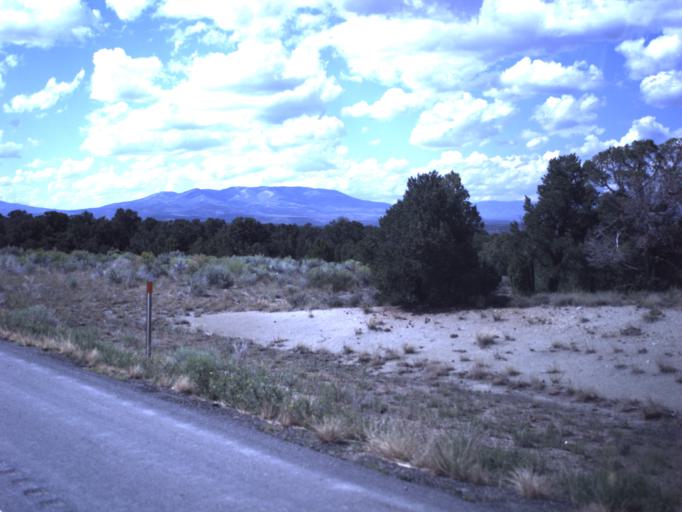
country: US
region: Utah
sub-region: Duchesne County
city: Duchesne
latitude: 40.1849
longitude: -110.6667
